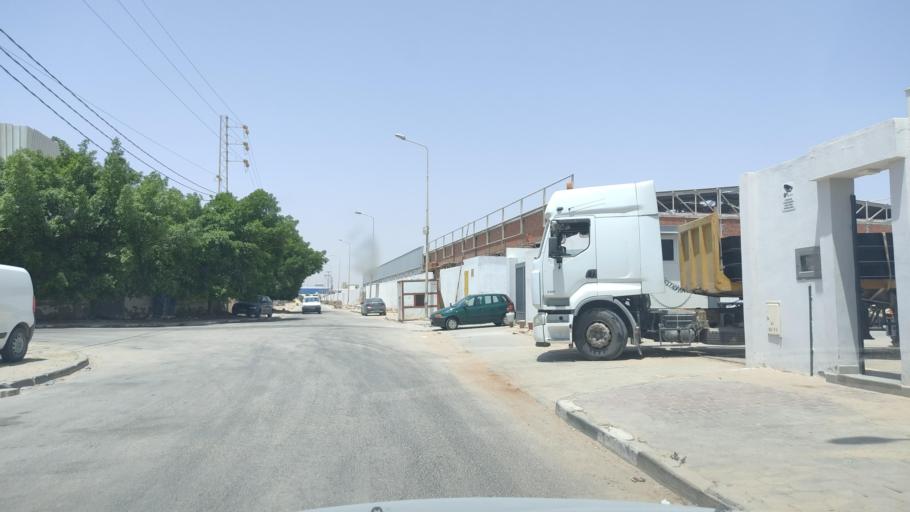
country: TN
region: Safaqis
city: Sfax
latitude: 34.6630
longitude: 10.7004
